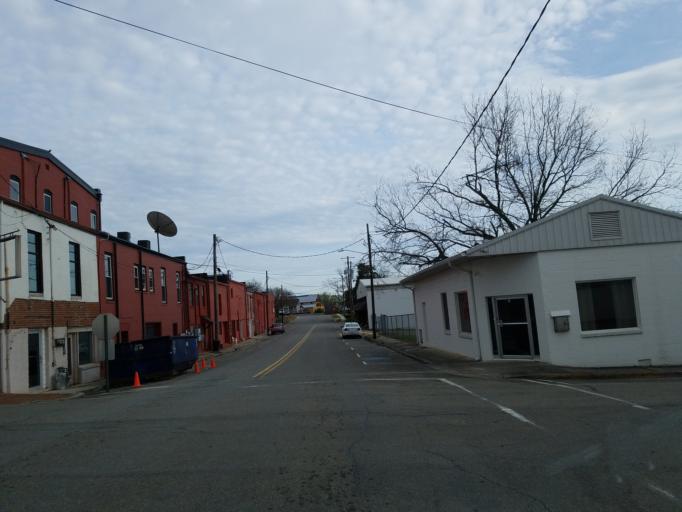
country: US
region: Georgia
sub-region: Pickens County
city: Jasper
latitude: 34.4688
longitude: -84.4310
